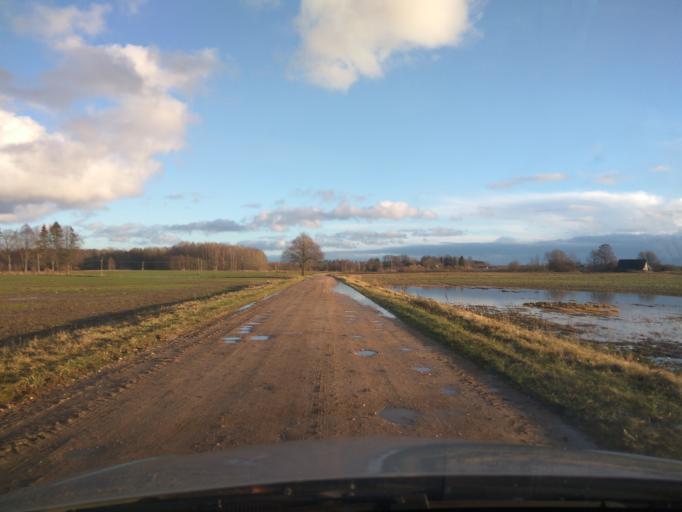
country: LV
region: Aizpute
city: Aizpute
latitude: 56.7729
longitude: 21.6985
